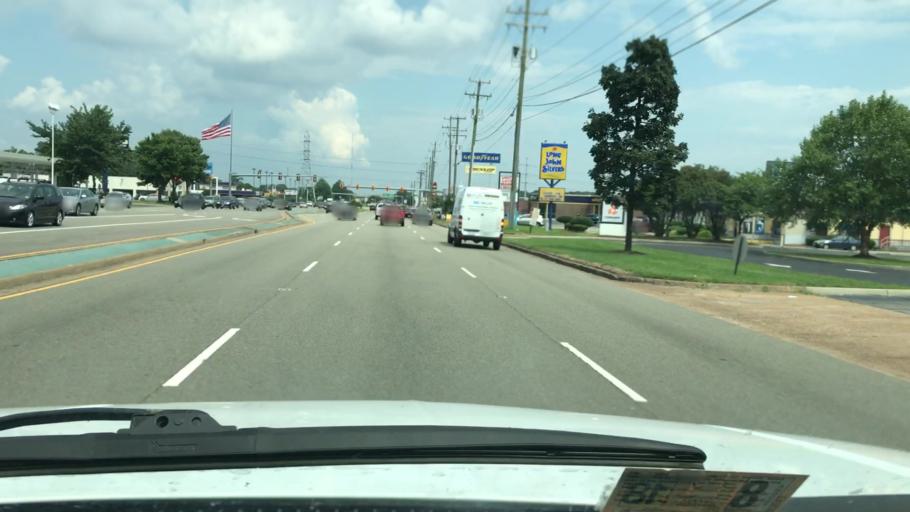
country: US
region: Virginia
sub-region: Chesterfield County
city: Bon Air
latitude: 37.4993
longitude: -77.5364
